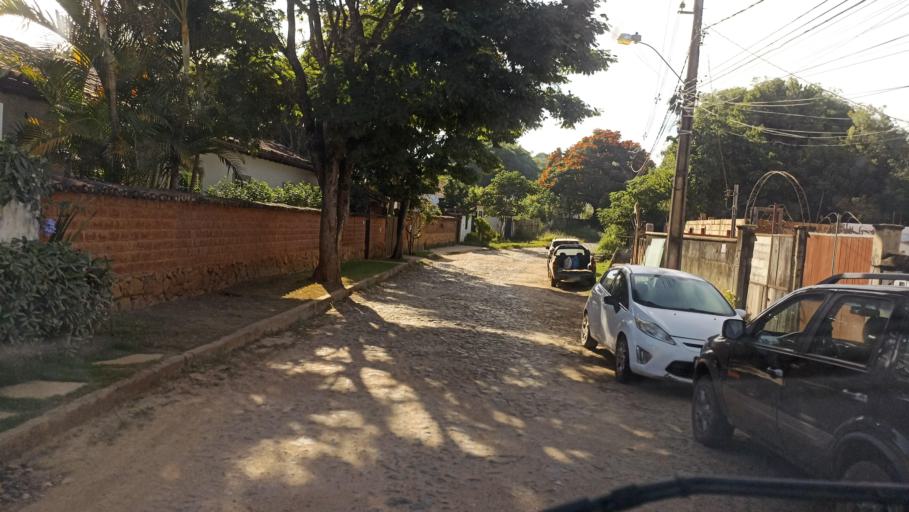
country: BR
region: Minas Gerais
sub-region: Tiradentes
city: Tiradentes
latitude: -21.1130
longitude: -44.1870
